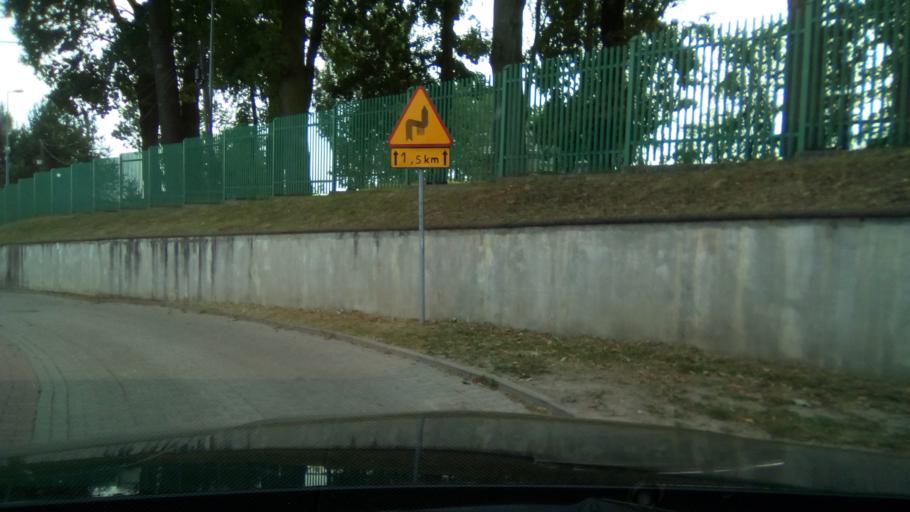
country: PL
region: Lesser Poland Voivodeship
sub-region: Krakow
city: Krakow
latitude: 50.0519
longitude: 19.8949
